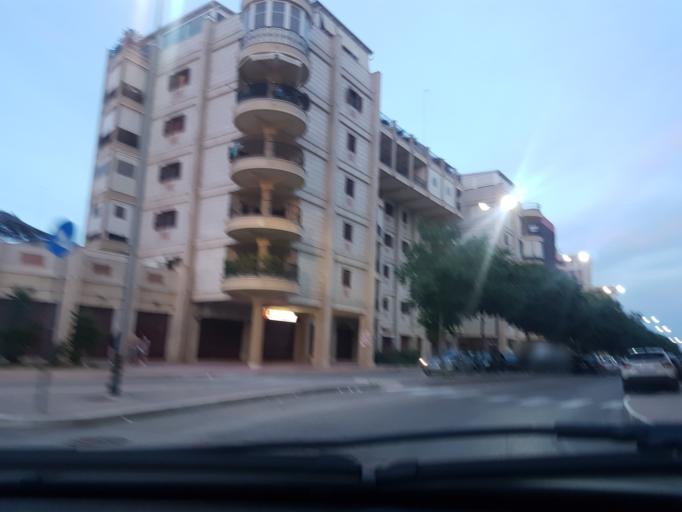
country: IT
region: Apulia
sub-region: Provincia di Barletta - Andria - Trani
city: Barletta
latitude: 41.3081
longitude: 16.2666
